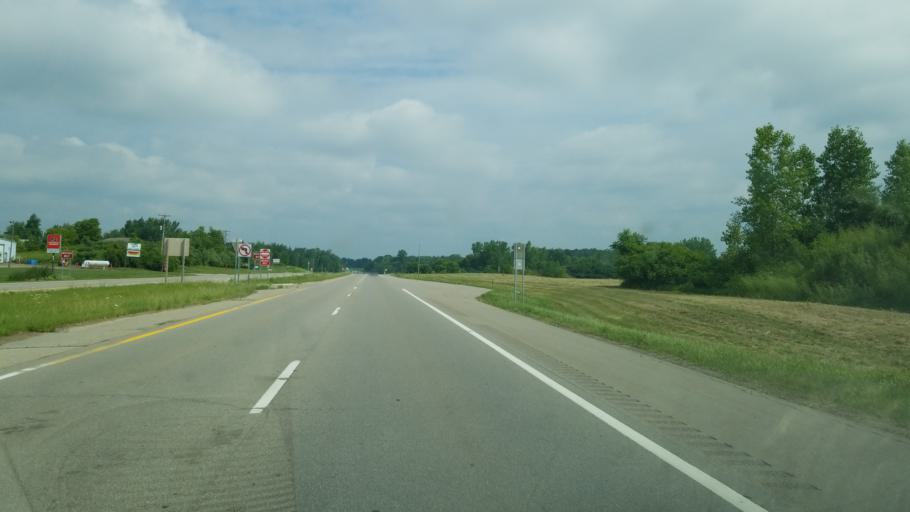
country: US
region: Michigan
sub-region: Kent County
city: Comstock Park
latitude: 43.0812
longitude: -85.6900
